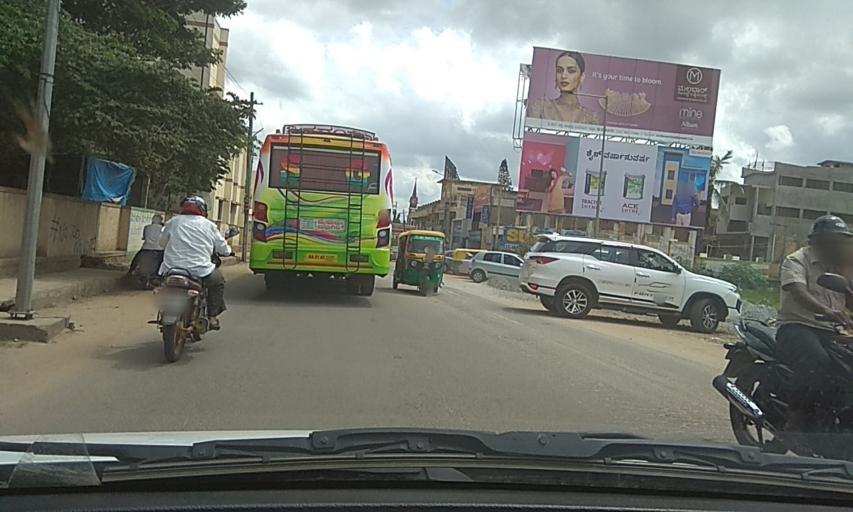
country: IN
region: Karnataka
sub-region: Tumkur
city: Tumkur
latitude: 13.3461
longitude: 77.1019
